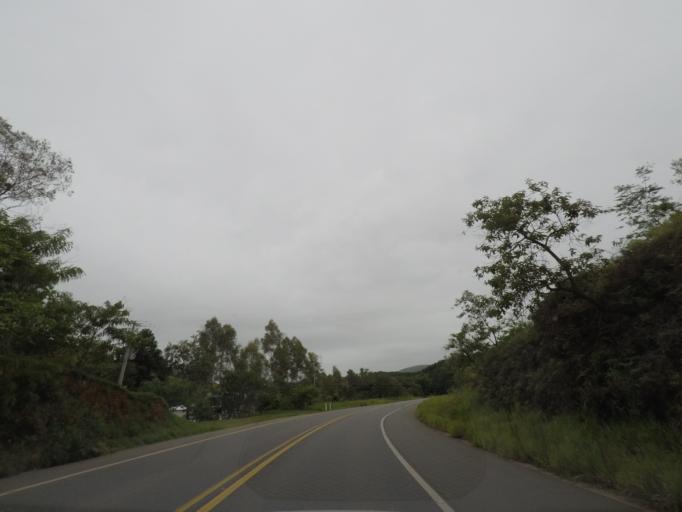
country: BR
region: Sao Paulo
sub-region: Cunha
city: Cunha
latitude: -23.0564
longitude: -44.9960
